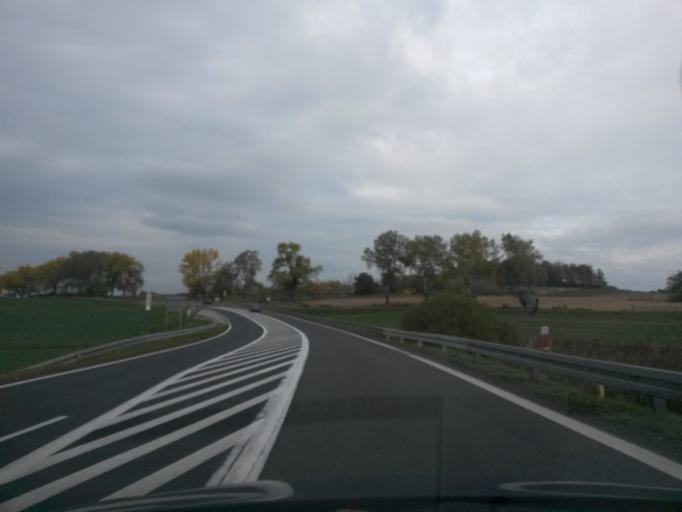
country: PL
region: Lower Silesian Voivodeship
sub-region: Powiat dzierzoniowski
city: Niemcza
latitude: 50.6688
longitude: 16.8310
